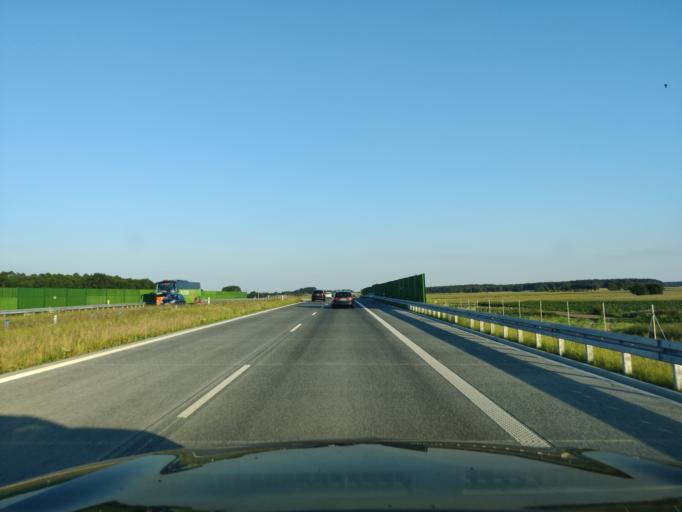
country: PL
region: Masovian Voivodeship
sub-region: Powiat mlawski
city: Strzegowo
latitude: 52.8754
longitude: 20.2754
